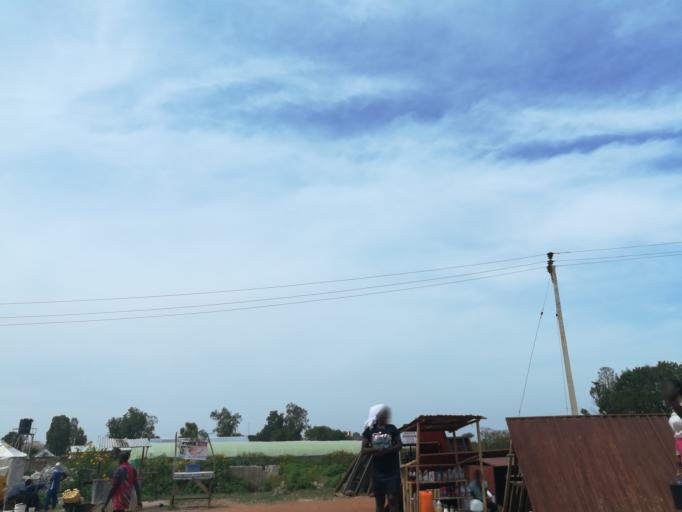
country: NG
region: Plateau
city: Jos
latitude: 9.8704
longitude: 8.8496
